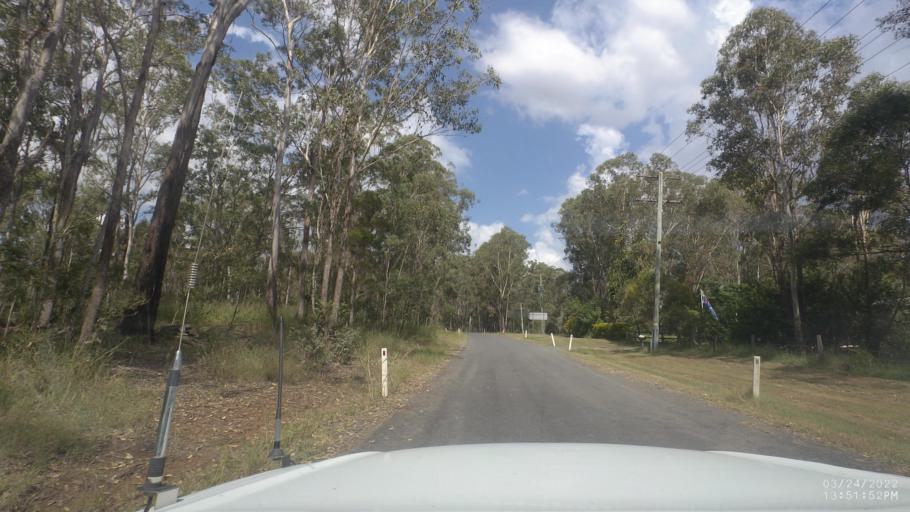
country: AU
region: Queensland
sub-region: Logan
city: Chambers Flat
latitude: -27.7732
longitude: 153.1188
